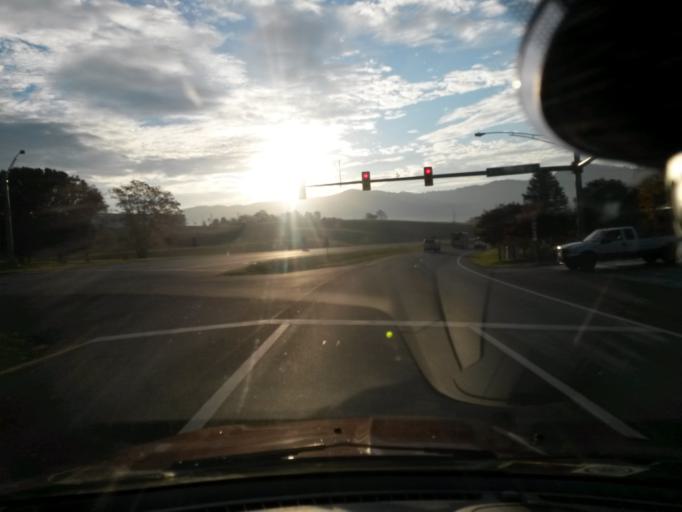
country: US
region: Virginia
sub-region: Botetourt County
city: Laymantown
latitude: 37.3425
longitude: -79.8781
